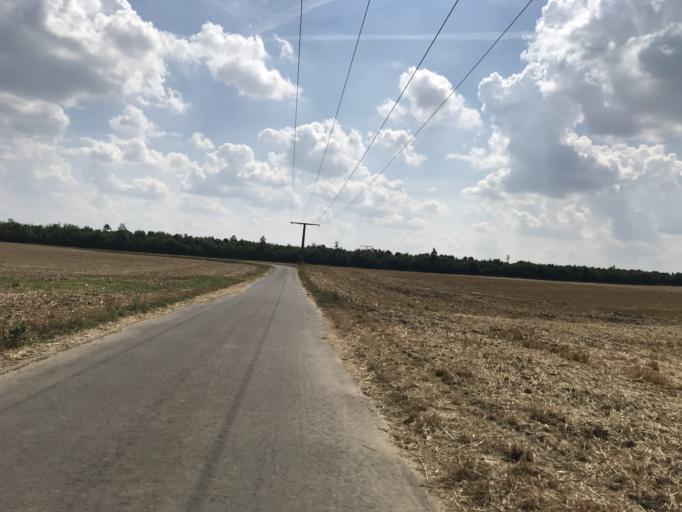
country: DE
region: Hesse
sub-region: Regierungsbezirk Darmstadt
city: Wolfersheim
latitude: 50.4215
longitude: 8.8356
